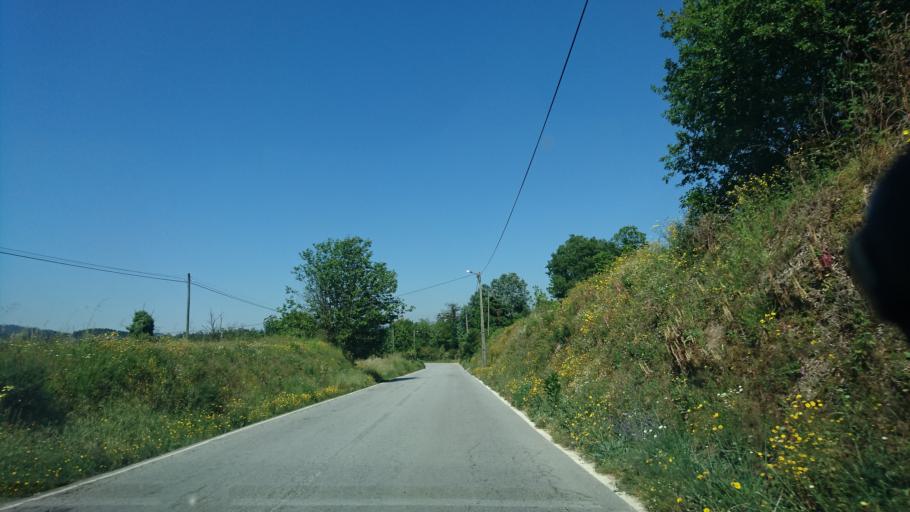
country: PT
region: Porto
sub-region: Paredes
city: Baltar
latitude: 41.1624
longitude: -8.3559
